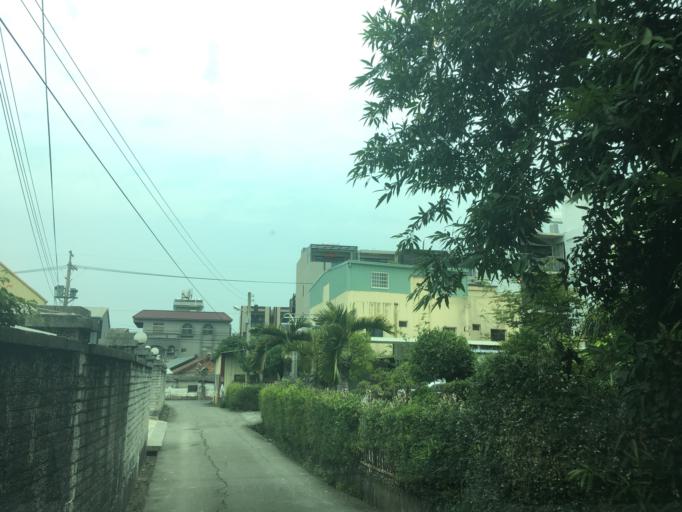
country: TW
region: Taiwan
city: Zhongxing New Village
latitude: 24.0374
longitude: 120.6903
